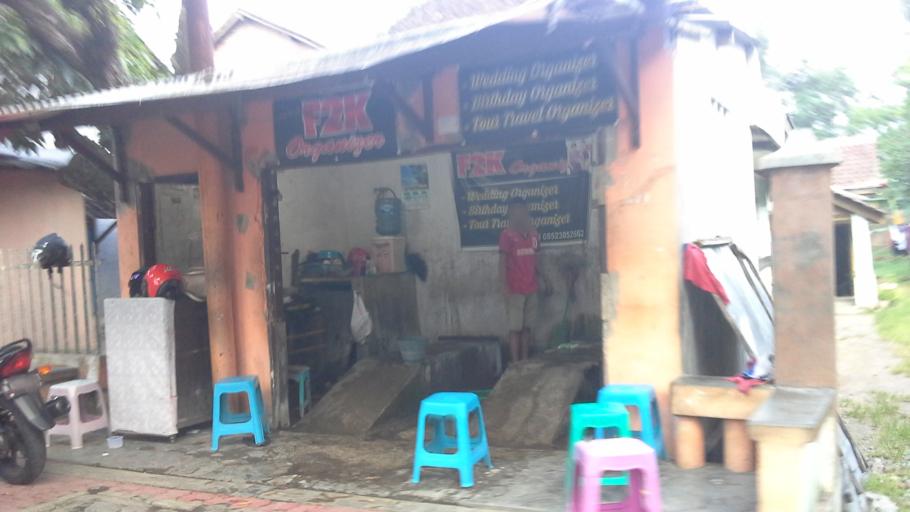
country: ID
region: East Java
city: Bondowoso
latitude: -7.9194
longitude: 113.8214
